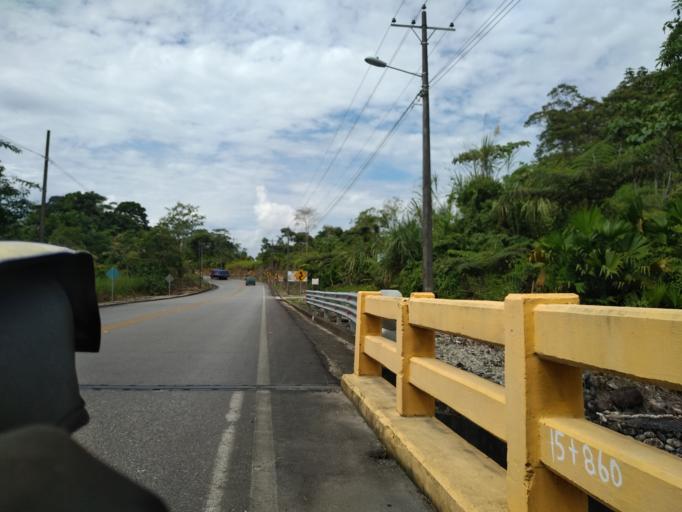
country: EC
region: Napo
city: Tena
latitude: -1.1363
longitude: -77.8331
